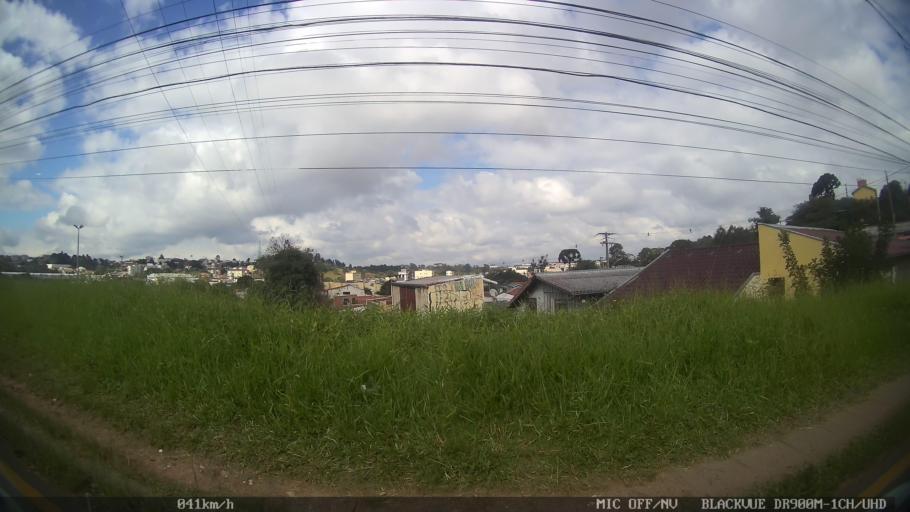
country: BR
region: Parana
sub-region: Pinhais
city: Pinhais
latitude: -25.3713
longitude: -49.2094
